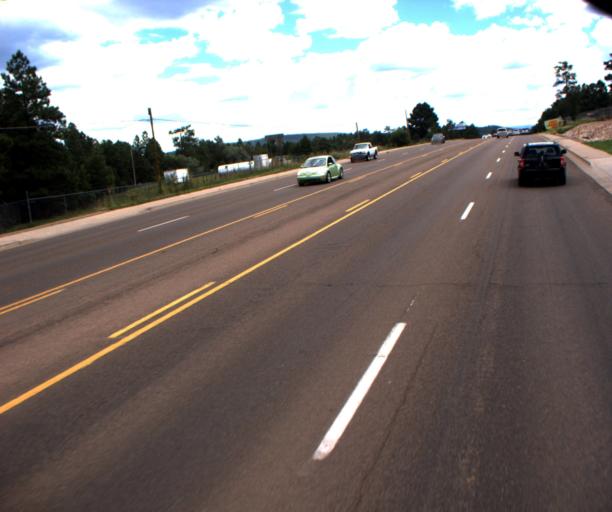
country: US
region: Arizona
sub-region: Navajo County
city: Lake of the Woods
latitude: 34.1657
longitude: -109.9927
